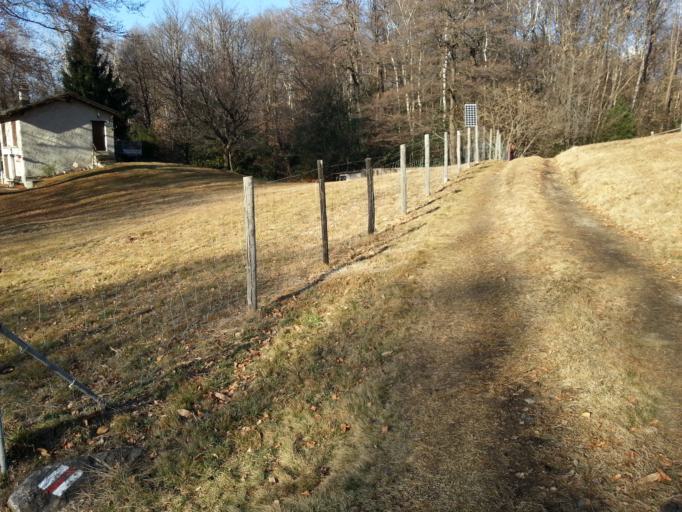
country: CH
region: Ticino
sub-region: Bellinzona District
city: Cadenazzo
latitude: 46.1385
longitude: 8.9235
